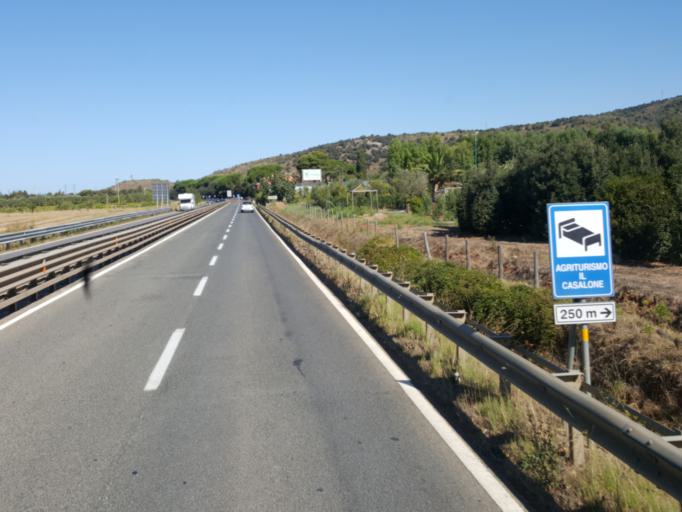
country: IT
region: Tuscany
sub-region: Provincia di Grosseto
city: Orbetello Scalo
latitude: 42.4340
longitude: 11.2818
